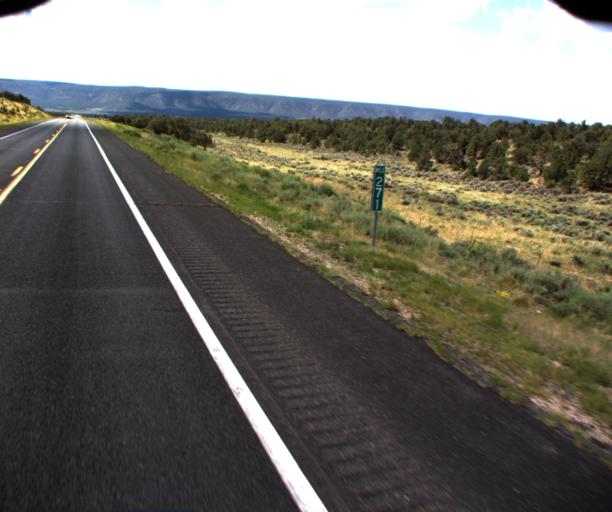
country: US
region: Arizona
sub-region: Coconino County
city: Grand Canyon
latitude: 35.9687
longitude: -111.7875
